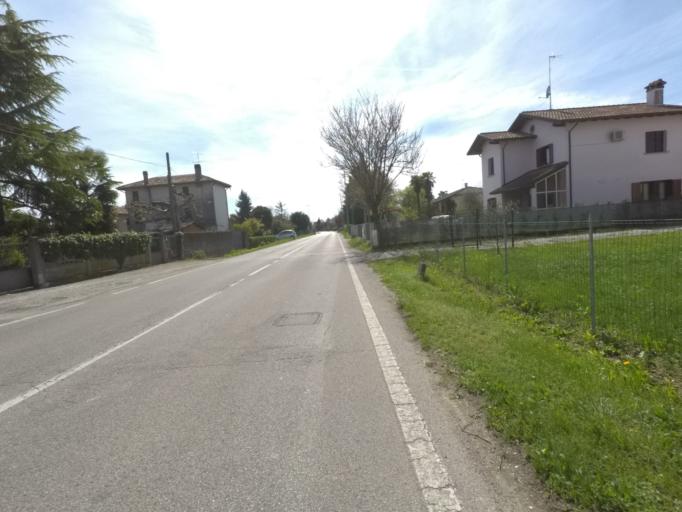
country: IT
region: Friuli Venezia Giulia
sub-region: Provincia di Pordenone
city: Fiume Veneto
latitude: 45.9335
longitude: 12.7385
